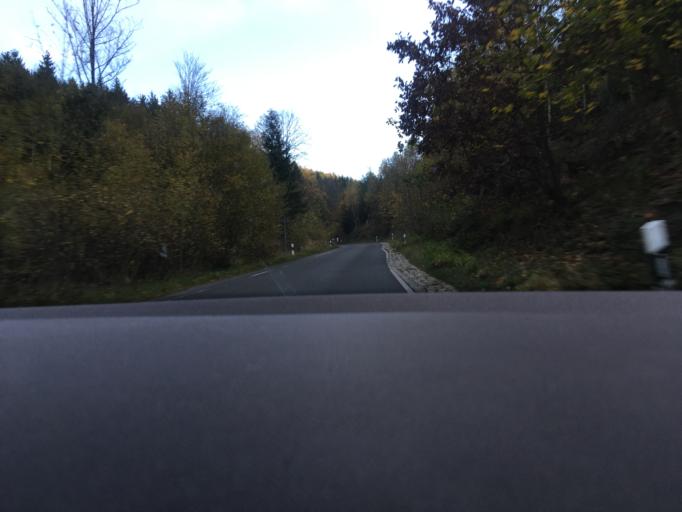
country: DE
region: Saxony
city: Glashutte
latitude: 50.8508
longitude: 13.7953
